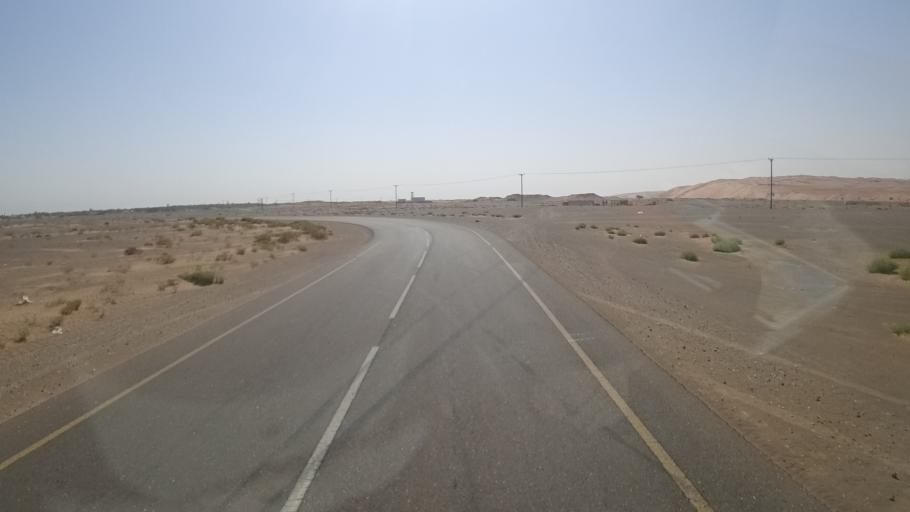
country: OM
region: Ash Sharqiyah
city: Al Qabil
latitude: 22.4985
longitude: 58.7265
